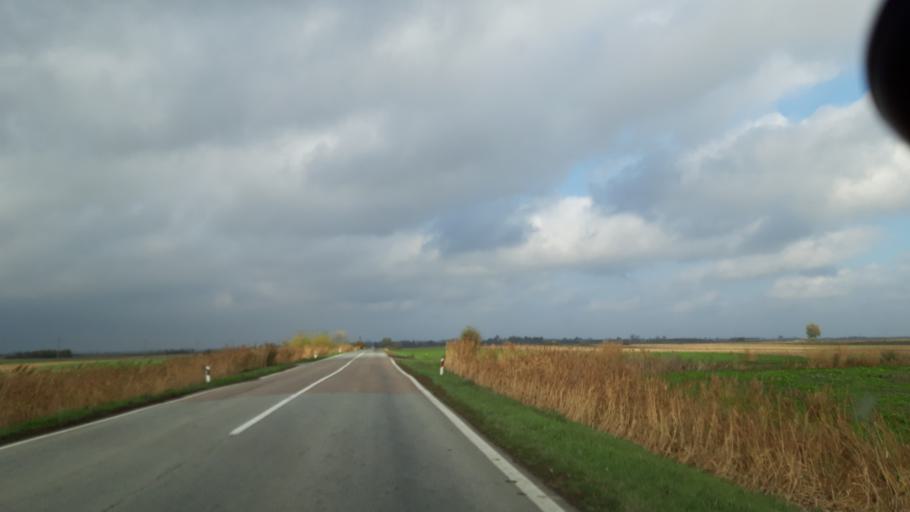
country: RS
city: Ostojicevo
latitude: 45.9114
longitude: 20.1522
